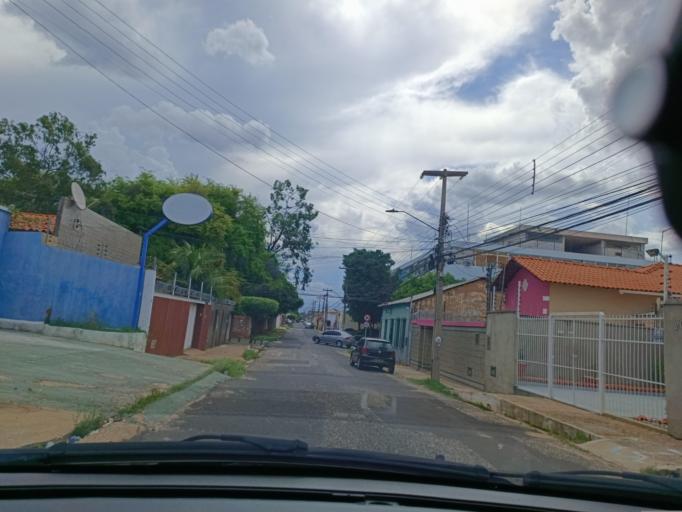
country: BR
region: Piaui
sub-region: Teresina
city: Teresina
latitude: -5.0827
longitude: -42.8094
